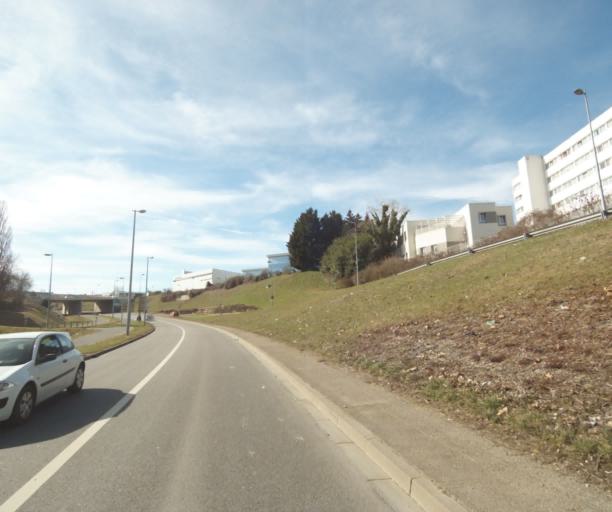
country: FR
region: Lorraine
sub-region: Departement de Meurthe-et-Moselle
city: Laxou
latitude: 48.6959
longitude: 6.1313
